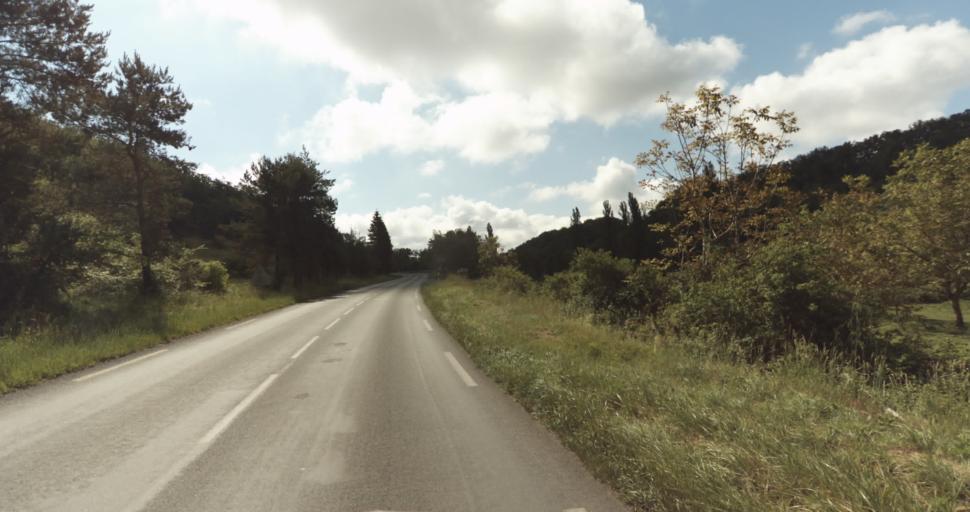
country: FR
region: Aquitaine
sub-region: Departement de la Dordogne
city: Lalinde
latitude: 44.8477
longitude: 0.8178
